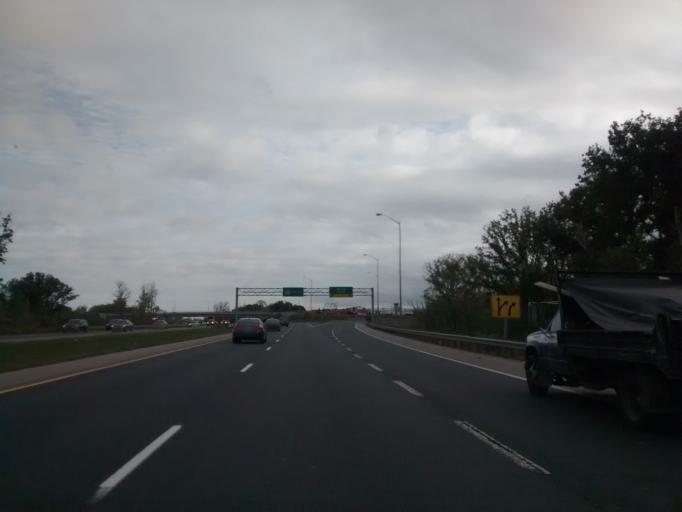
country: CA
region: Ontario
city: Hamilton
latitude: 43.2368
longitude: -79.7760
